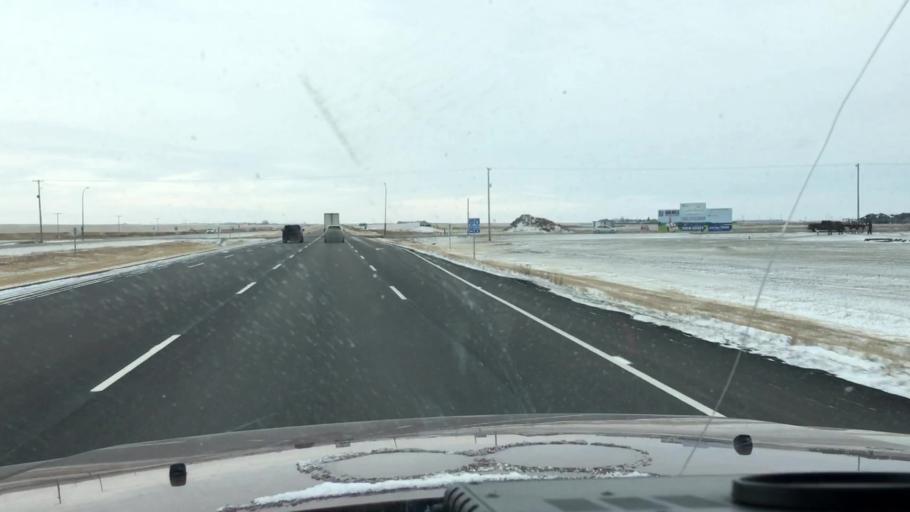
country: CA
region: Saskatchewan
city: Saskatoon
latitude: 51.8104
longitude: -106.4960
